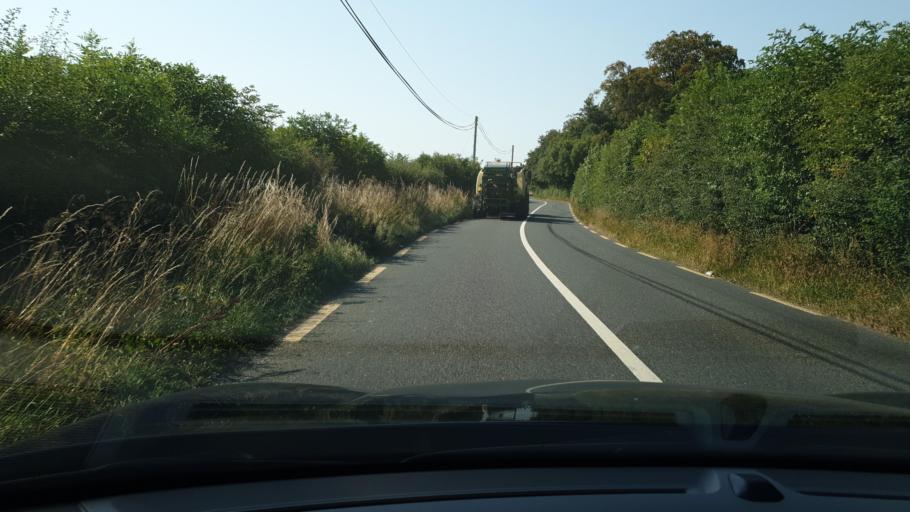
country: IE
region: Leinster
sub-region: An Mhi
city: Athboy
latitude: 53.6073
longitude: -6.8897
